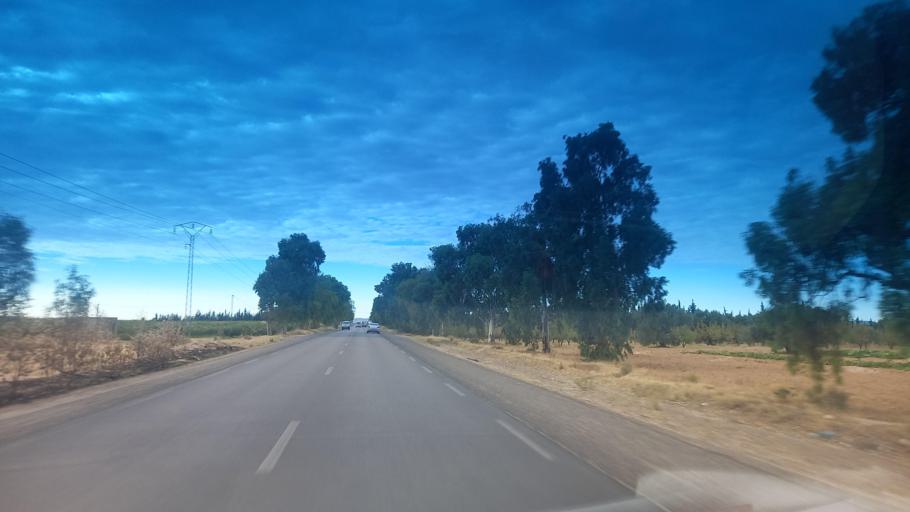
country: TN
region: Al Qasrayn
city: Sbiba
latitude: 35.2910
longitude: 9.0913
